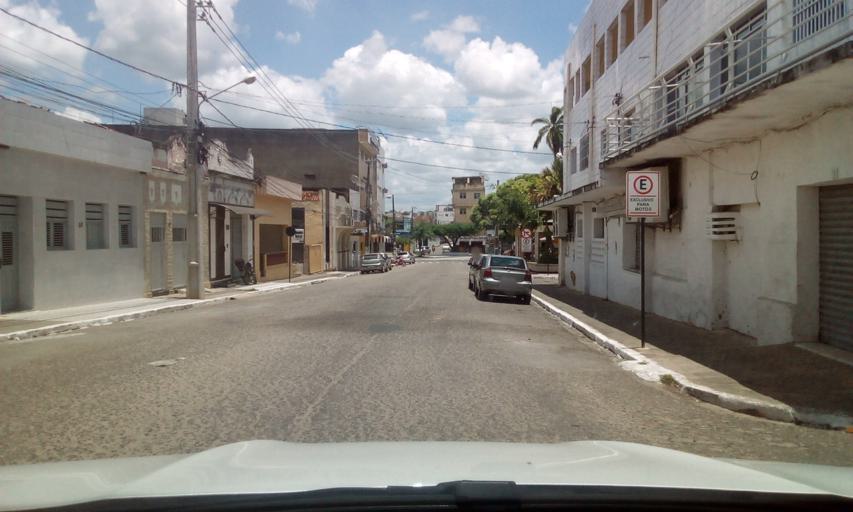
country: BR
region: Paraiba
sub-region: Guarabira
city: Guarabira
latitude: -6.8531
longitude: -35.4887
